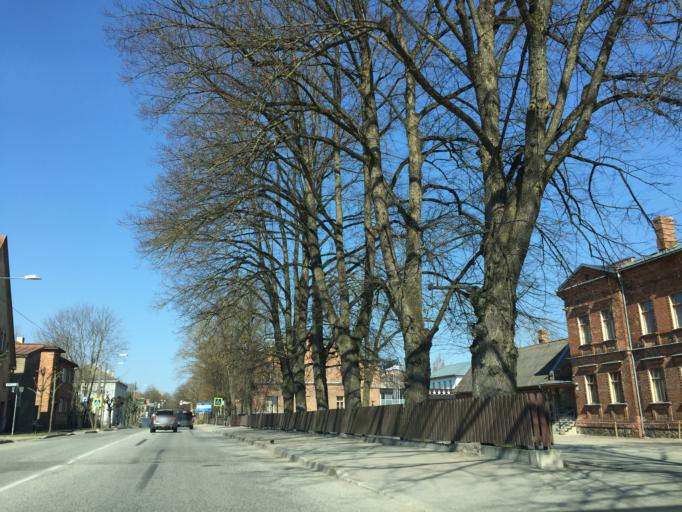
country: EE
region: Tartu
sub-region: Tartu linn
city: Tartu
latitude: 58.3886
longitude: 26.7314
